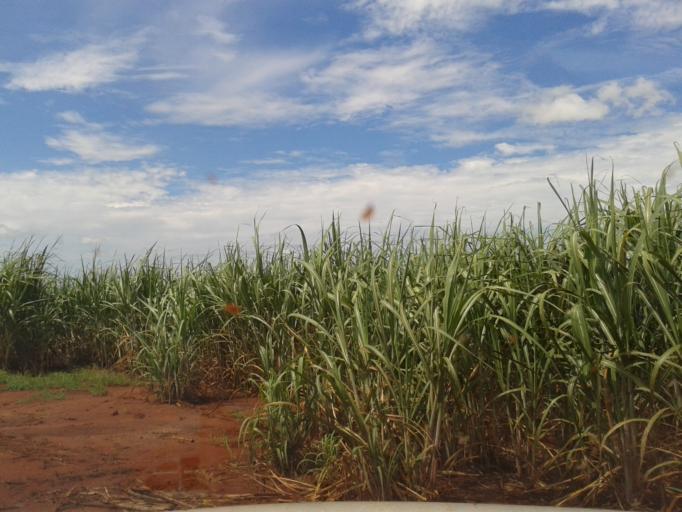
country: BR
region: Minas Gerais
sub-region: Santa Vitoria
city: Santa Vitoria
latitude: -19.2095
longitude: -50.6345
